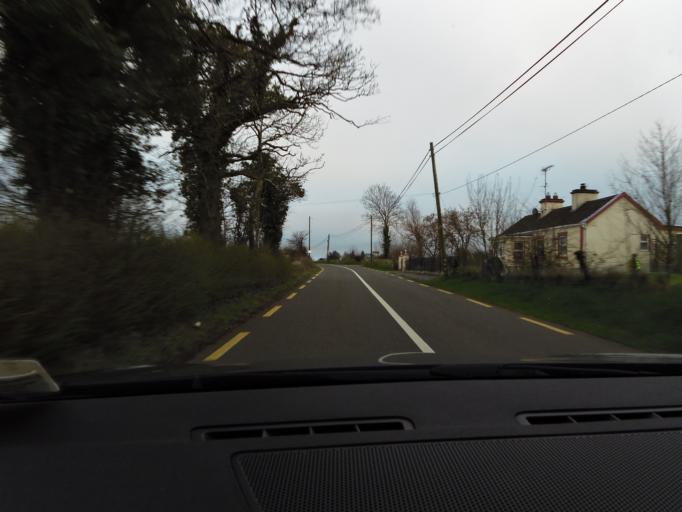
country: IE
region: Connaught
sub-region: Sligo
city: Ballymote
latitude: 54.0073
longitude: -8.5459
